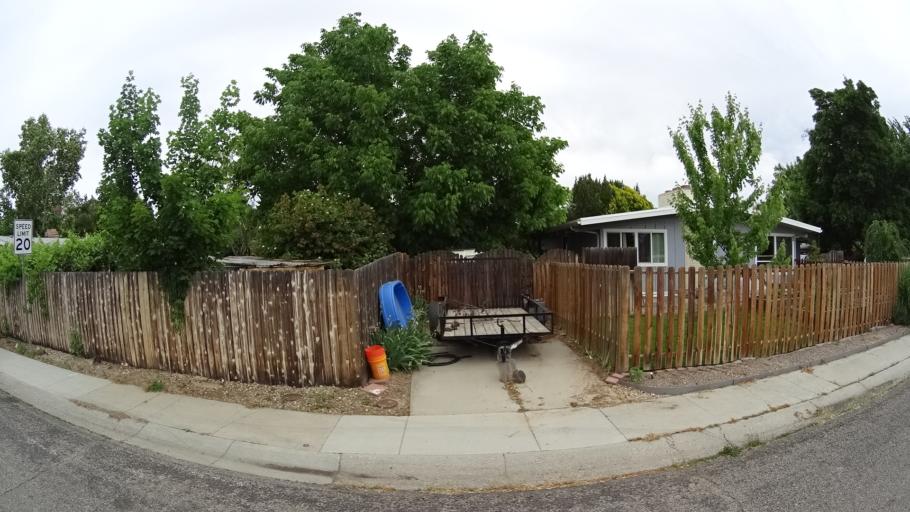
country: US
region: Idaho
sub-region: Ada County
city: Boise
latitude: 43.5772
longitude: -116.2041
